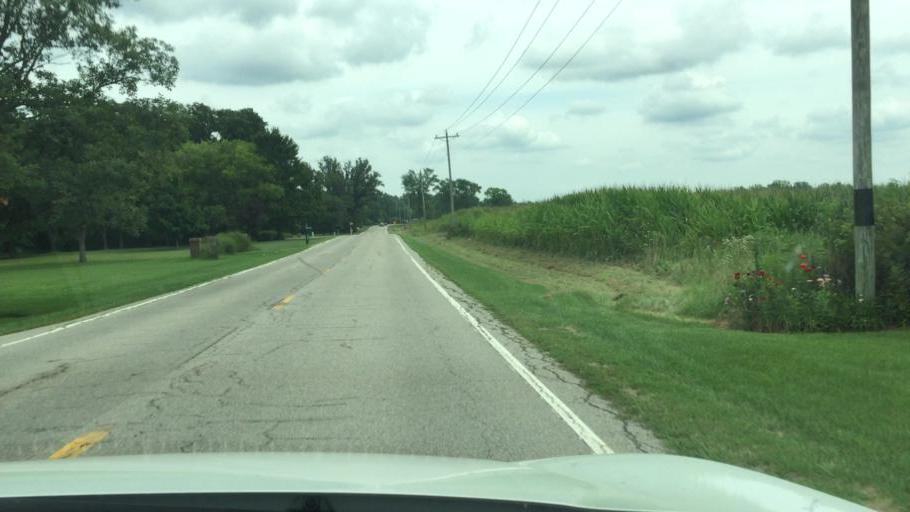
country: US
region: Ohio
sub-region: Champaign County
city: North Lewisburg
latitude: 40.2358
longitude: -83.4686
